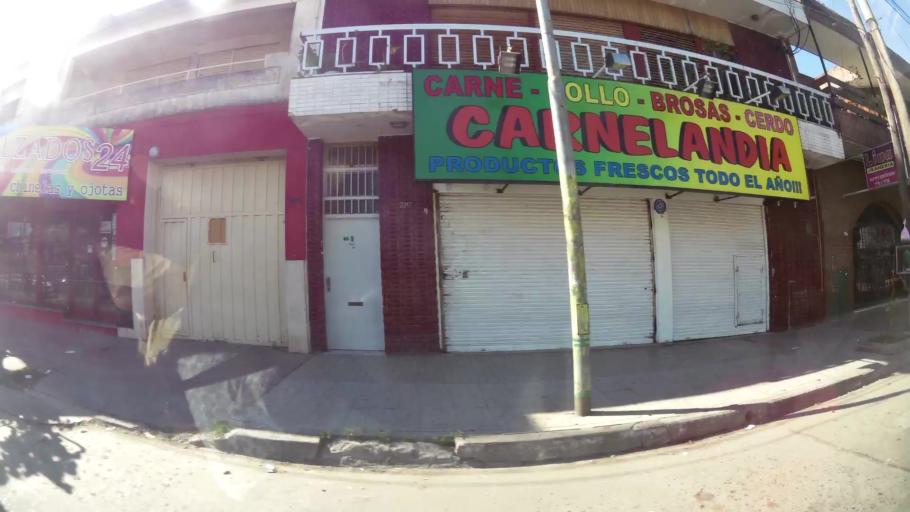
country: AR
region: Cordoba
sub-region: Departamento de Capital
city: Cordoba
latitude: -31.4105
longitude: -64.1541
